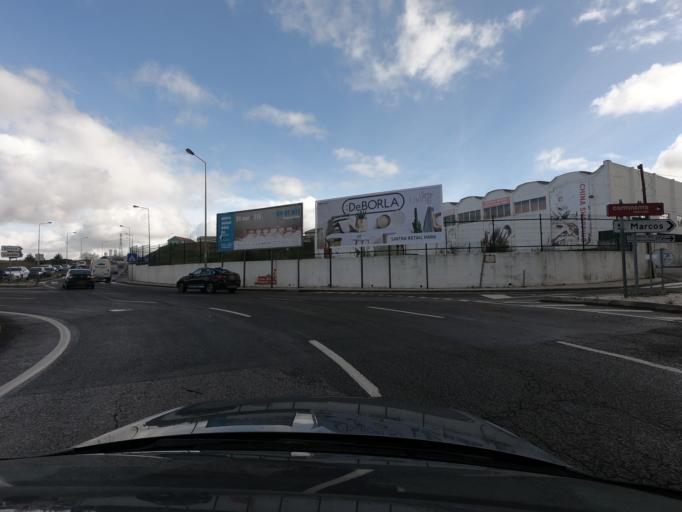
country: PT
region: Lisbon
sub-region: Sintra
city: Cacem
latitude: 38.7509
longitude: -9.3057
